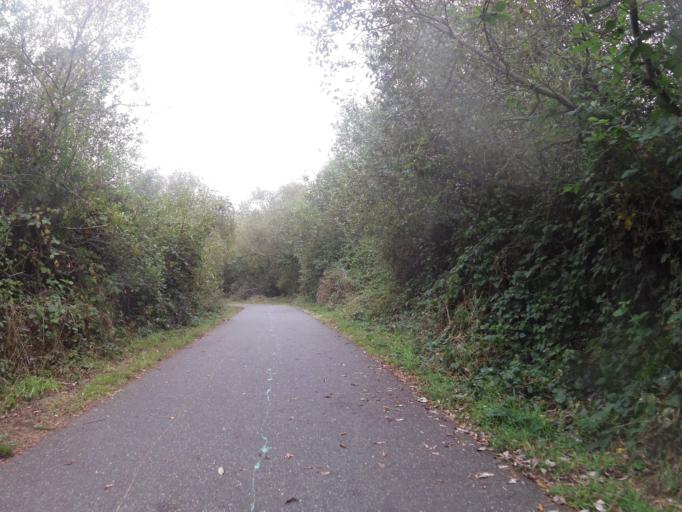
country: US
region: California
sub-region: Humboldt County
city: Bayview
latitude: 40.7669
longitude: -124.1967
